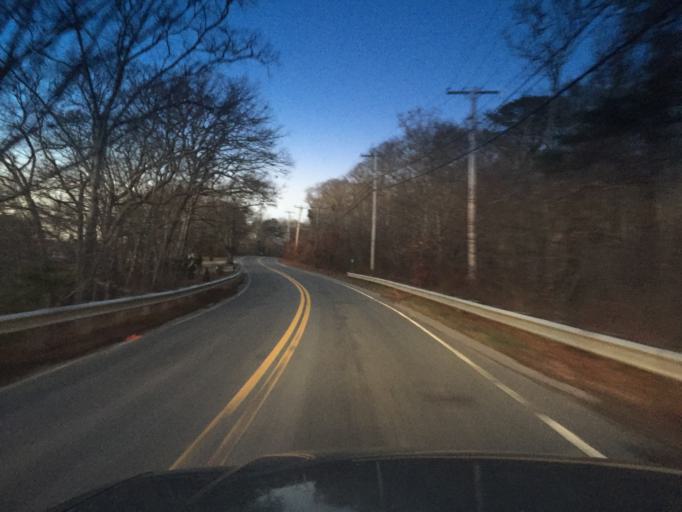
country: US
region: Massachusetts
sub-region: Barnstable County
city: West Falmouth
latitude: 41.6212
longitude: -70.6226
